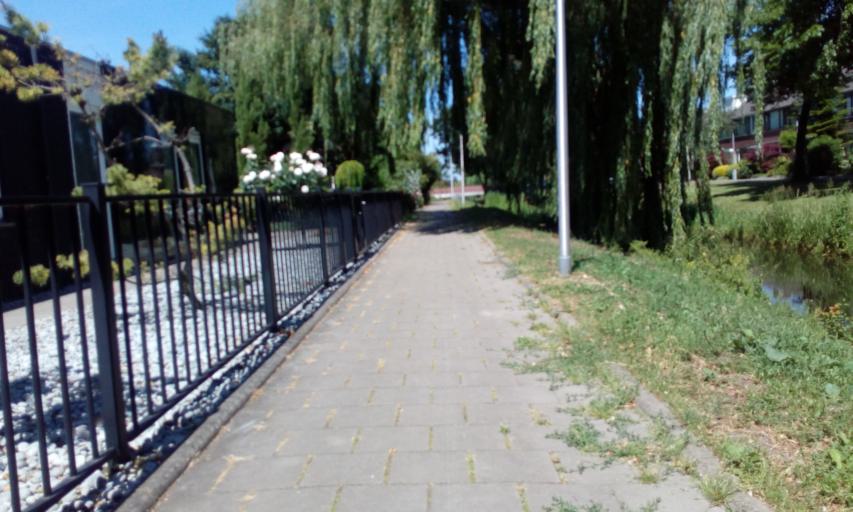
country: NL
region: South Holland
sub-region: Gemeente Lansingerland
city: Bleiswijk
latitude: 52.0068
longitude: 4.5349
